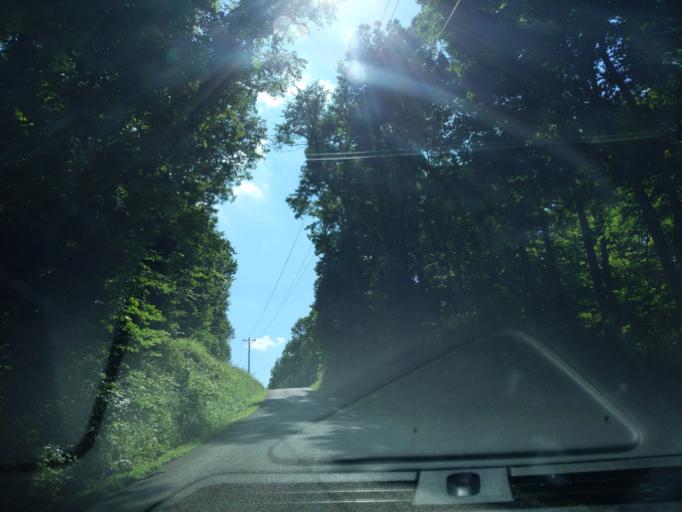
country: US
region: Indiana
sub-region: Ripley County
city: Osgood
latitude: 39.1903
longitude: -85.4113
